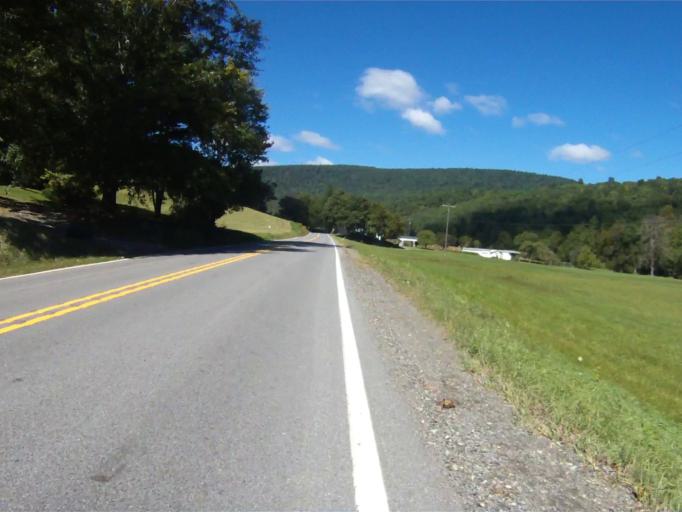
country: US
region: Pennsylvania
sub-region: Centre County
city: Milesburg
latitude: 40.9277
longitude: -77.9045
